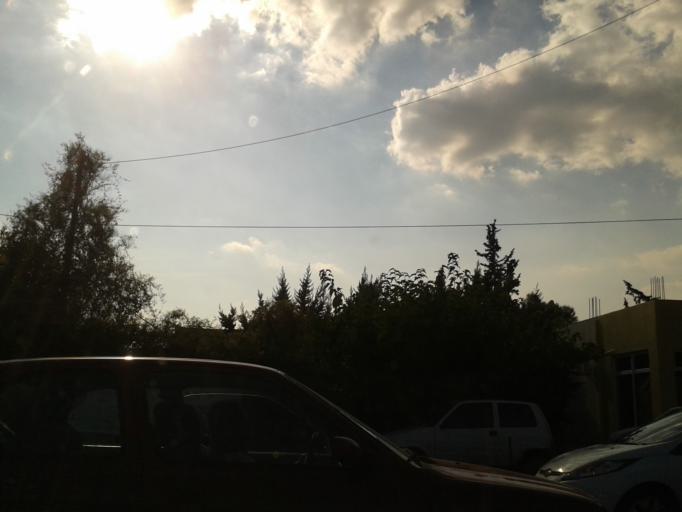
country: GR
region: Attica
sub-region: Nomarchia Anatolikis Attikis
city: Anoixi
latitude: 38.1357
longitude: 23.8572
